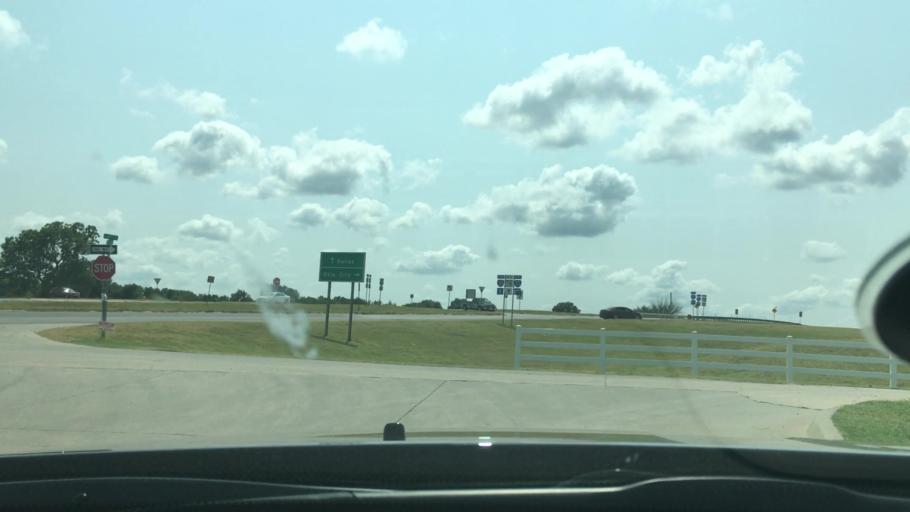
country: US
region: Oklahoma
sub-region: Murray County
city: Davis
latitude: 34.5070
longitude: -97.1713
